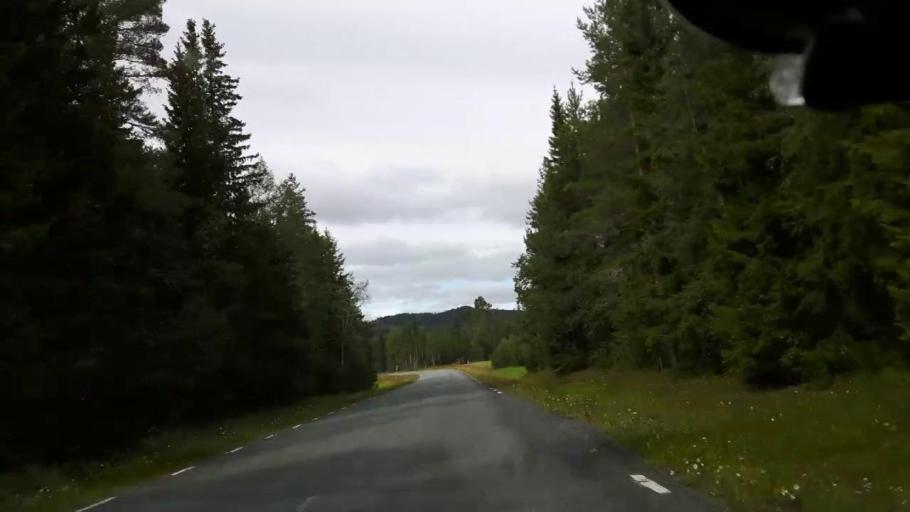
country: SE
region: Jaemtland
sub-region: Krokoms Kommun
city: Valla
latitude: 63.4802
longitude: 13.9759
